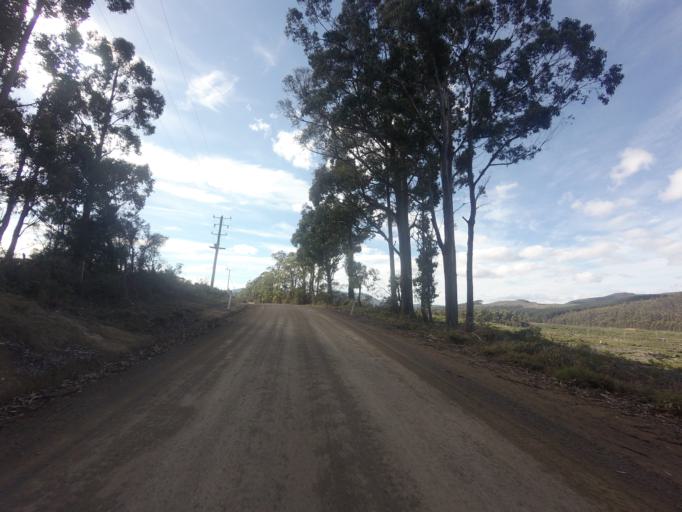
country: AU
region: Tasmania
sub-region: Clarence
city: Sandford
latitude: -43.1675
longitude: 147.7679
